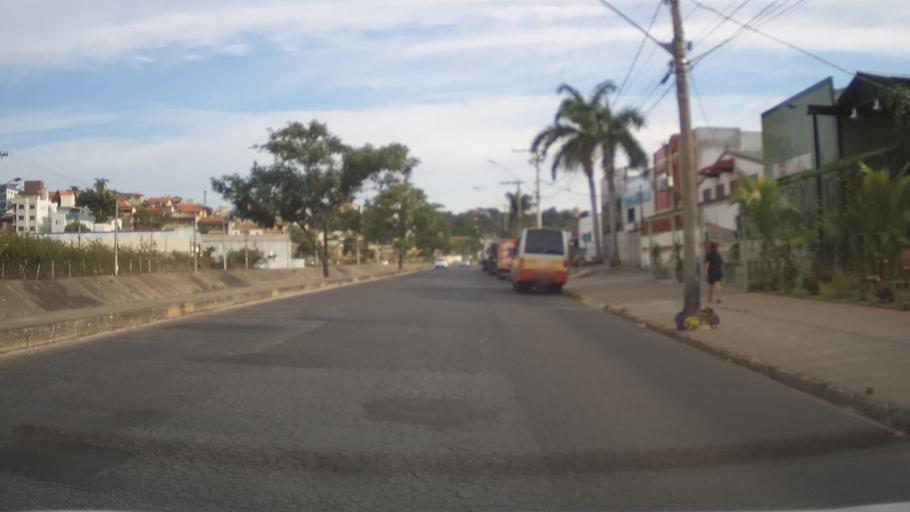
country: BR
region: Minas Gerais
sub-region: Contagem
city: Contagem
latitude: -19.8818
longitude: -44.0057
